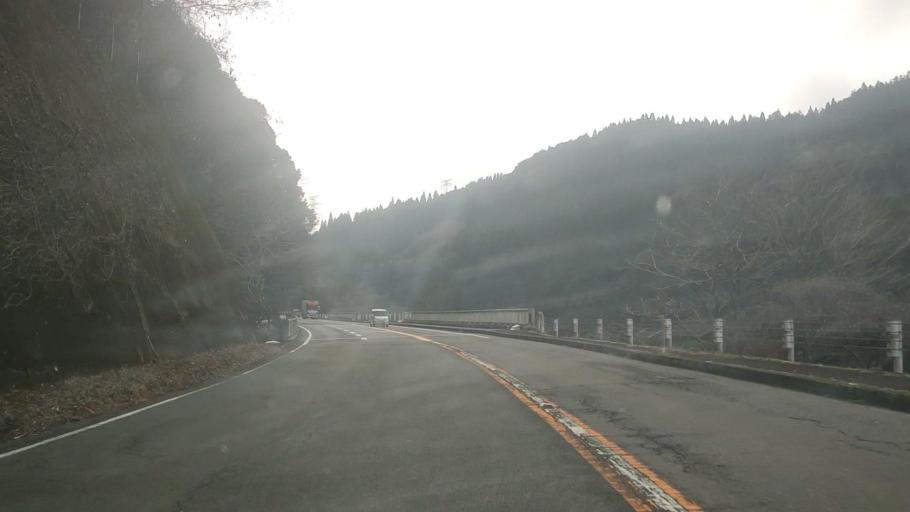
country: JP
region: Kumamoto
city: Hitoyoshi
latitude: 32.1156
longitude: 130.8065
